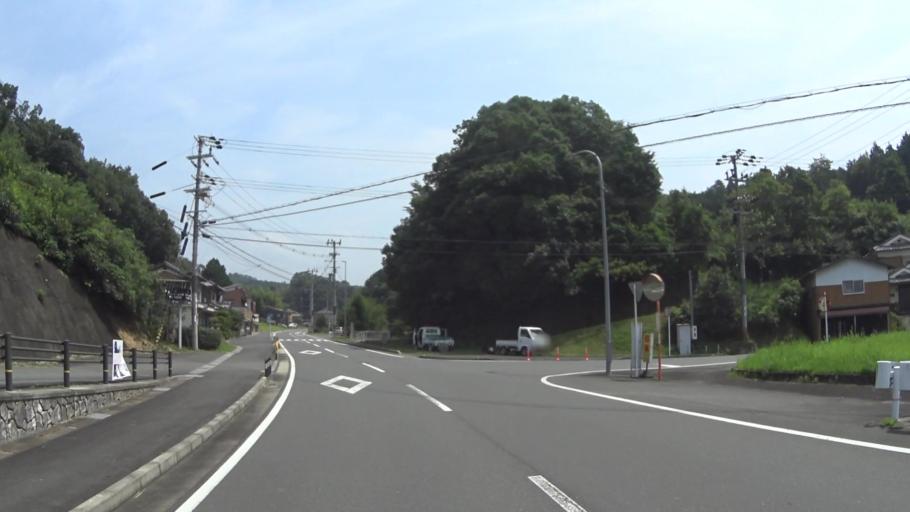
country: JP
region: Kyoto
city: Kameoka
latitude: 35.1776
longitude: 135.4439
